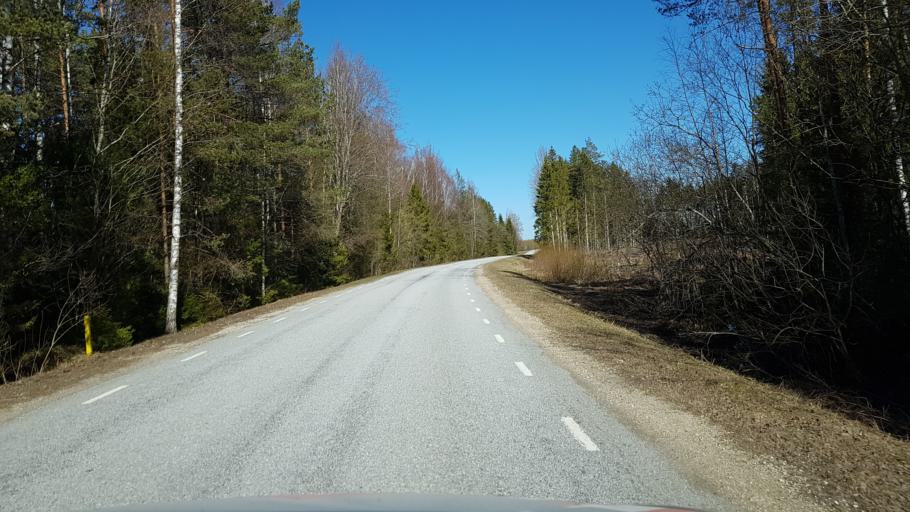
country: EE
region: Laeaene-Virumaa
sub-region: Viru-Nigula vald
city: Kunda
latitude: 59.3307
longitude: 26.6270
